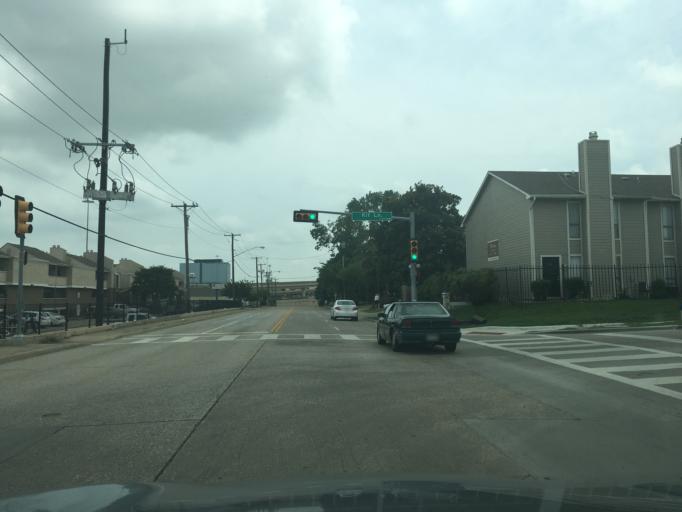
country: US
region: Texas
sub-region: Dallas County
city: Richardson
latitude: 32.9308
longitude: -96.7612
